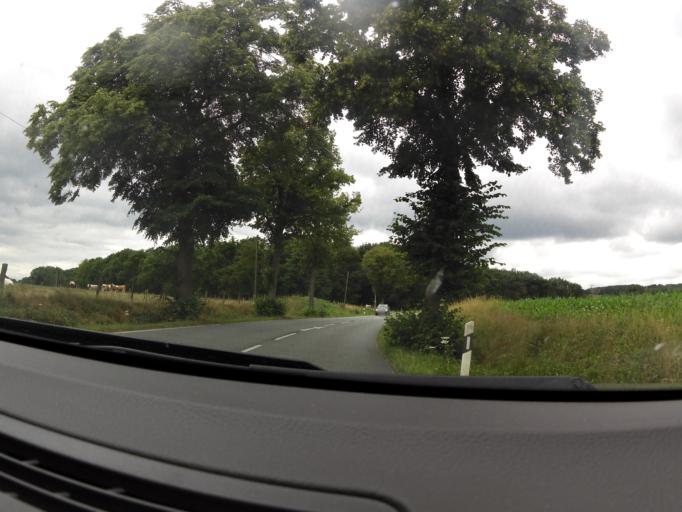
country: DE
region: North Rhine-Westphalia
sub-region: Regierungsbezirk Dusseldorf
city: Sonsbeck
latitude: 51.6121
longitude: 6.4123
